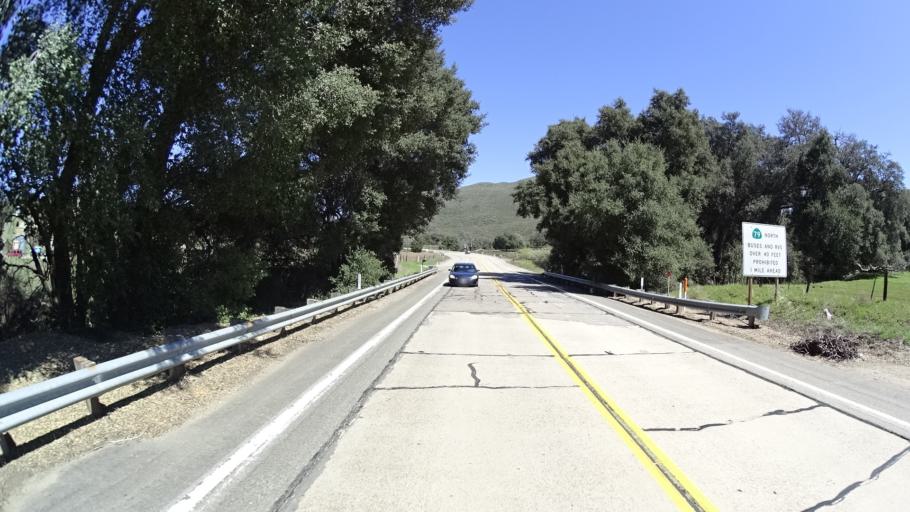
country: US
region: California
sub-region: San Diego County
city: Descanso
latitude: 32.8428
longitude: -116.6041
